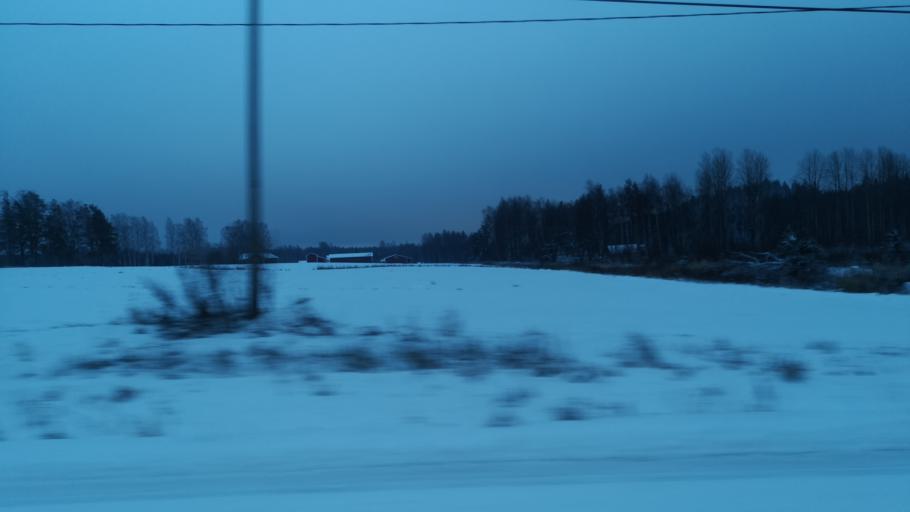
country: FI
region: Southern Savonia
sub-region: Savonlinna
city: Enonkoski
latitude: 62.0642
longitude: 28.7323
